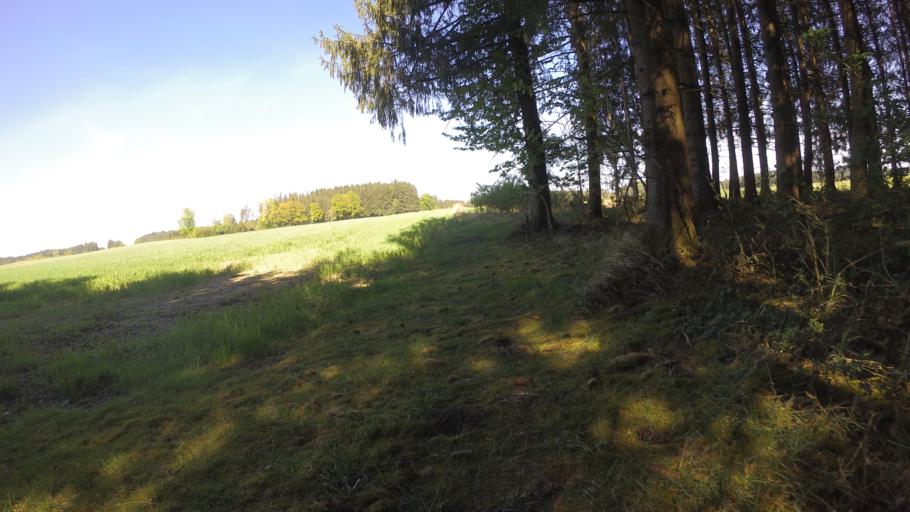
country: DE
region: Bavaria
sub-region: Upper Bavaria
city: Traunreut
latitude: 47.9508
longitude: 12.5409
